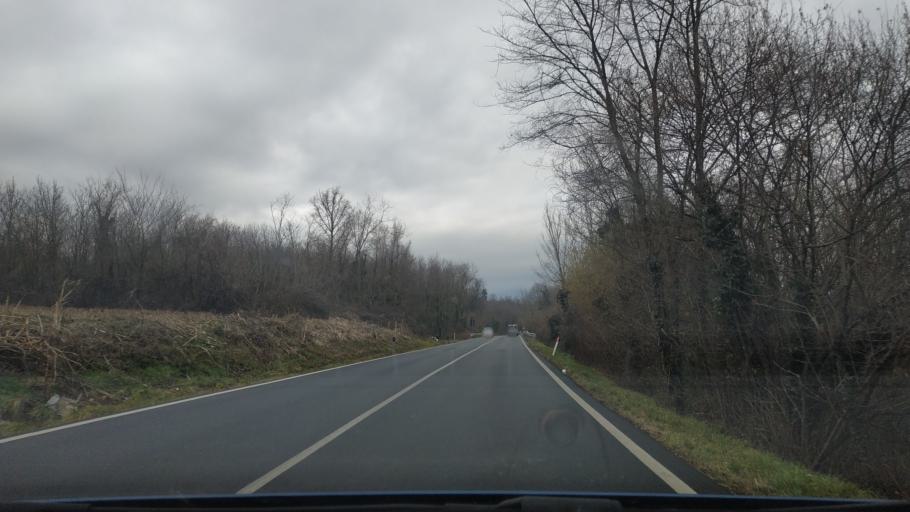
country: IT
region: Piedmont
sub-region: Provincia di Torino
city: Candia Canavese
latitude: 45.3393
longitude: 7.8881
